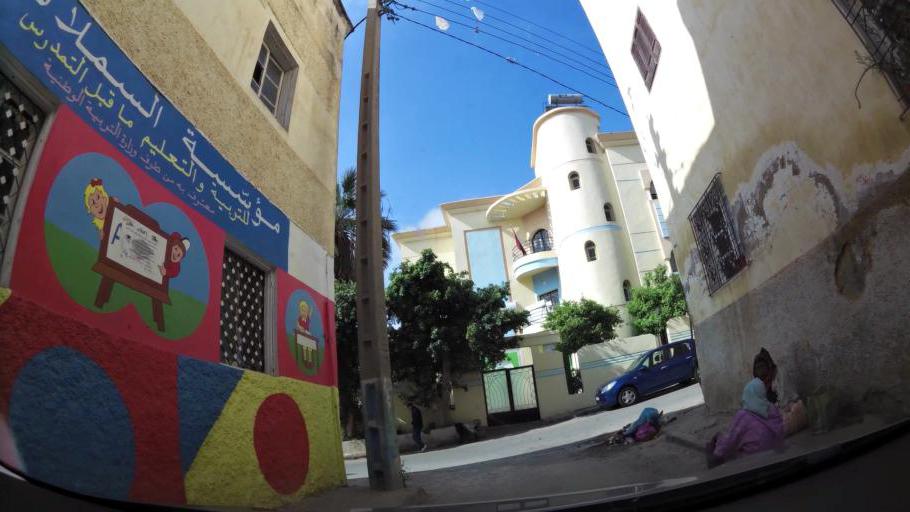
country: MA
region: Fes-Boulemane
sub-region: Fes
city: Fes
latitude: 34.0659
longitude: -5.0095
